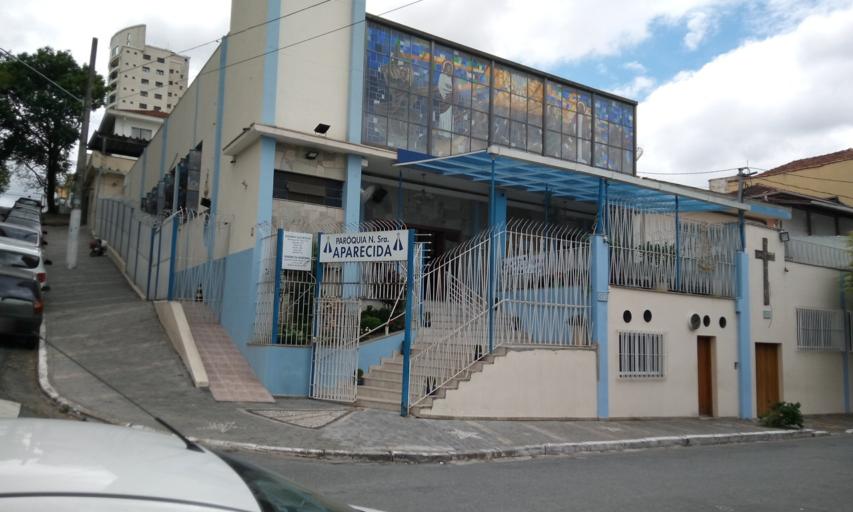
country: BR
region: Sao Paulo
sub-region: Sao Paulo
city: Sao Paulo
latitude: -23.4915
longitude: -46.6155
